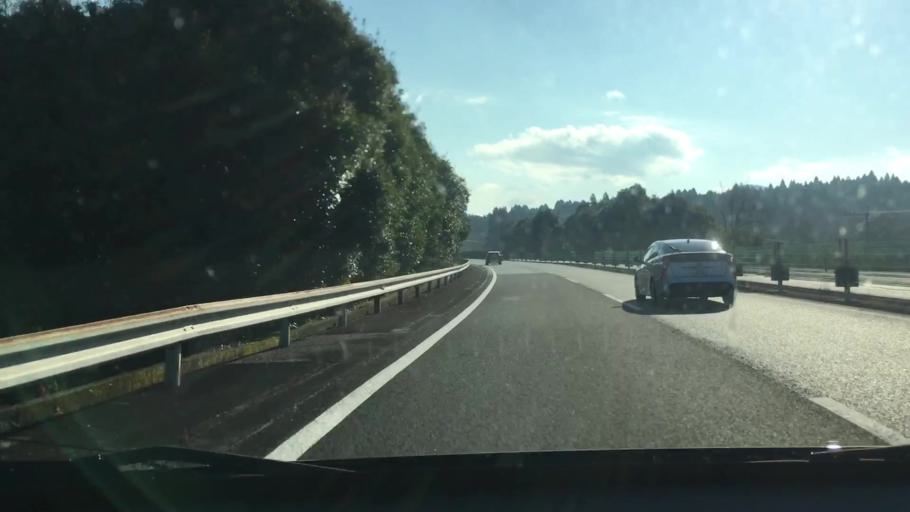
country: JP
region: Kagoshima
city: Okuchi-shinohara
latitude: 32.0104
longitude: 130.7566
